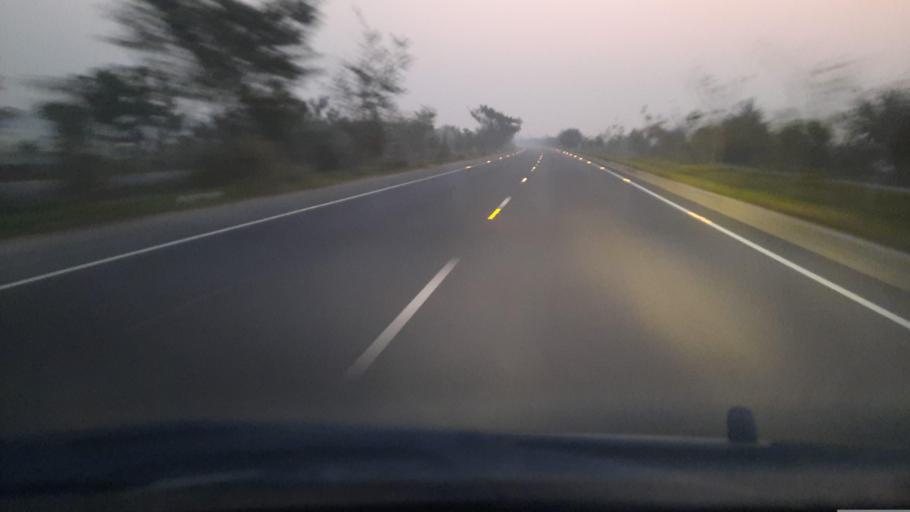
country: BD
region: Dhaka
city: Char Bhadrasan
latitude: 23.3976
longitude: 90.2287
